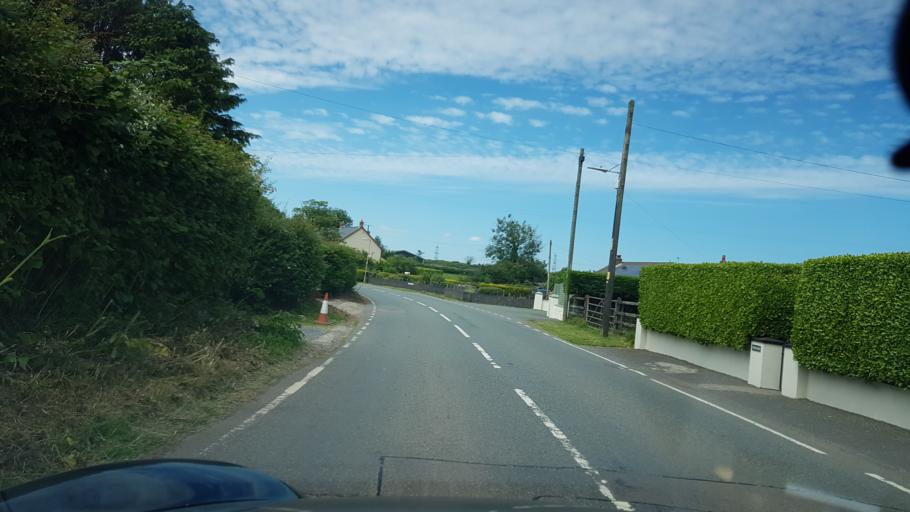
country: GB
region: Wales
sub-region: Carmarthenshire
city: Whitland
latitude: 51.7748
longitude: -4.6019
